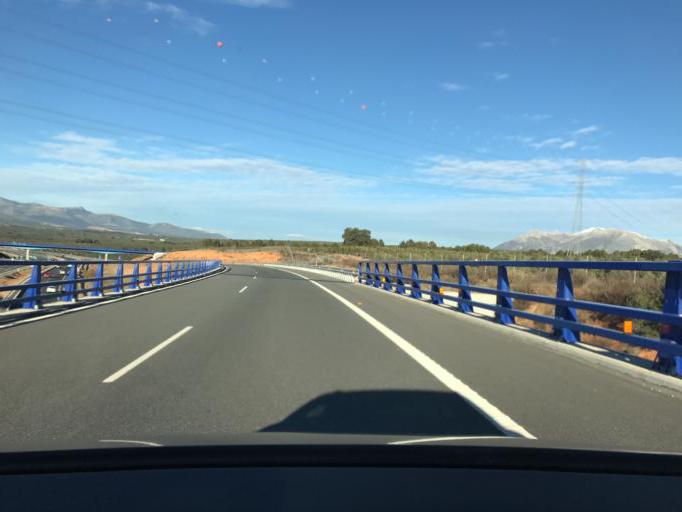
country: ES
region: Andalusia
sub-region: Provincia de Granada
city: Albolote
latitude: 37.2655
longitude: -3.6595
